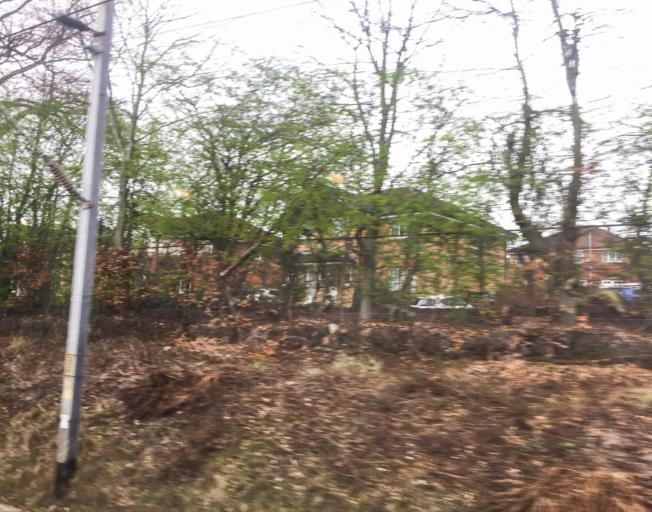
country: GB
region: Scotland
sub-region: West Dunbartonshire
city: Clydebank
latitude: 55.9089
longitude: -4.4123
